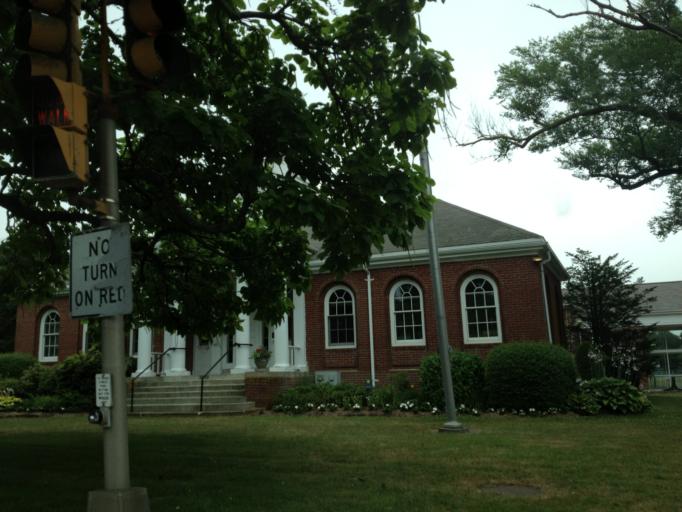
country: US
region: Massachusetts
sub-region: Barnstable County
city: Eastham
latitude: 41.8302
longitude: -69.9737
